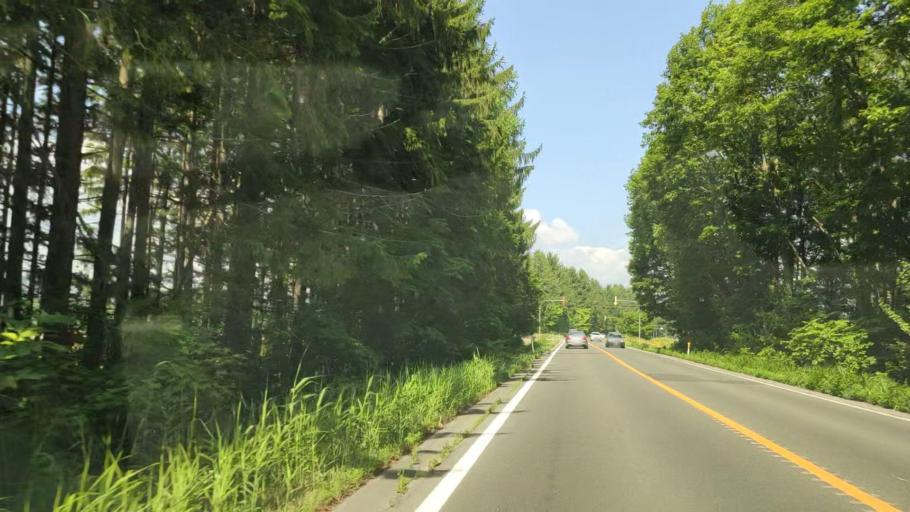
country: JP
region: Hokkaido
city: Shimo-furano
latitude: 43.5110
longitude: 142.4517
